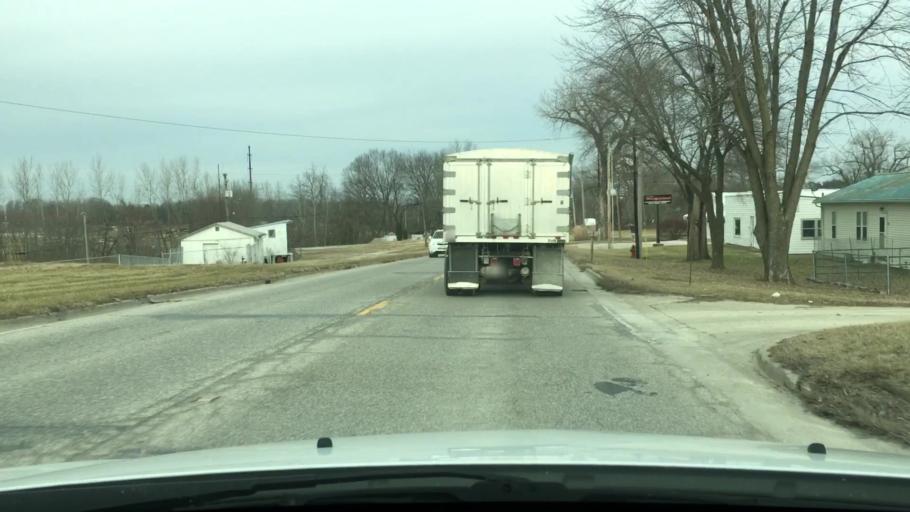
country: US
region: Illinois
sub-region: Pike County
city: Pittsfield
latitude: 39.6157
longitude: -90.8028
